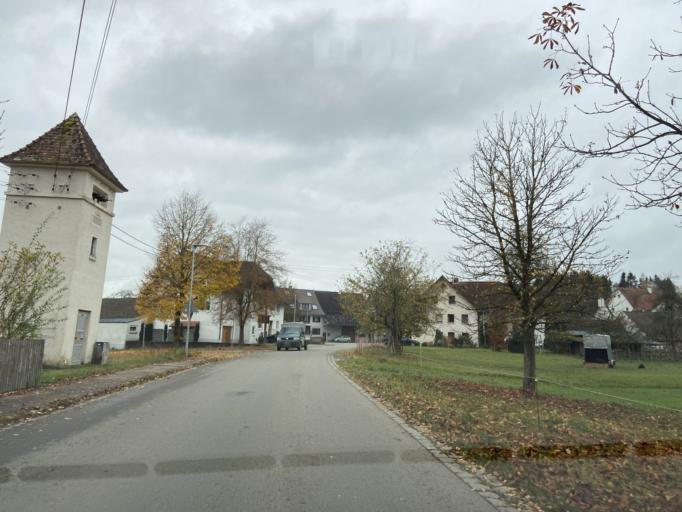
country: DE
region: Baden-Wuerttemberg
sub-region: Tuebingen Region
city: Messkirch
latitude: 48.0064
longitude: 9.1603
